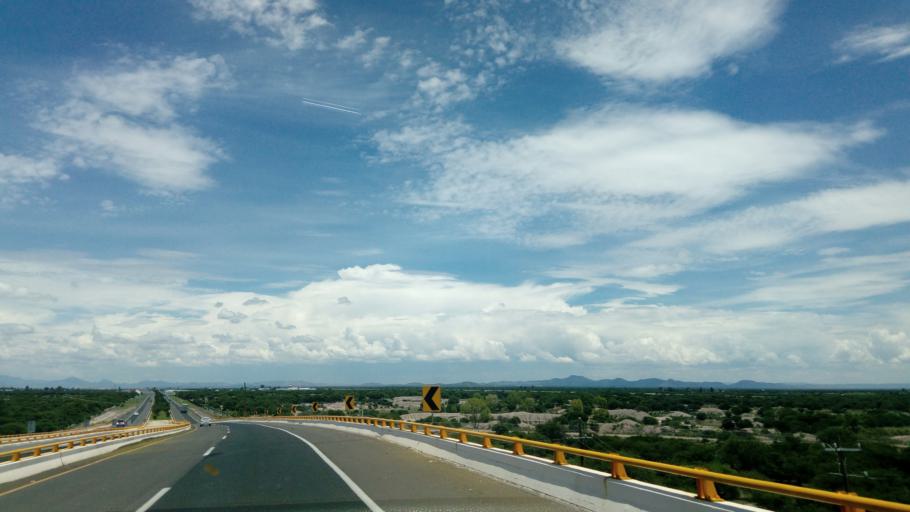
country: MX
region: Durango
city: Victoria de Durango
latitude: 24.1119
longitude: -104.5510
